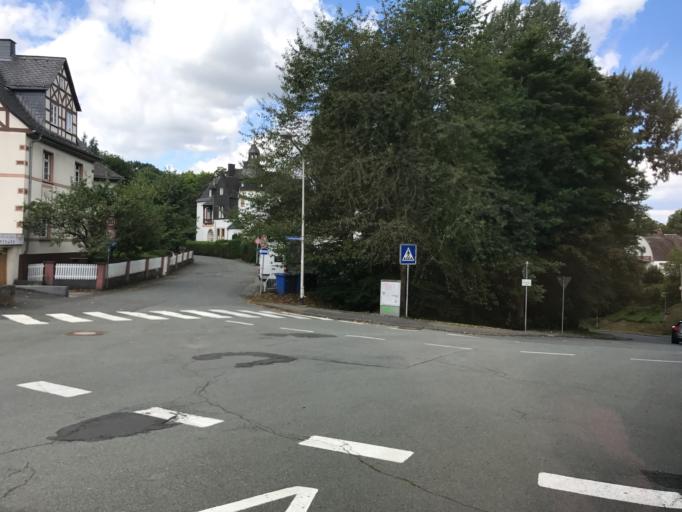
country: DE
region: Hesse
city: Weilburg
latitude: 50.4831
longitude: 8.2704
